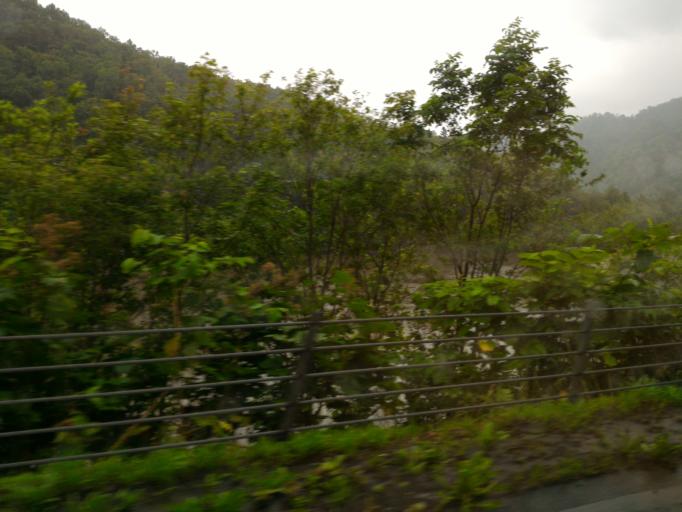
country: JP
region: Hokkaido
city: Nayoro
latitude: 44.7254
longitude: 142.1663
